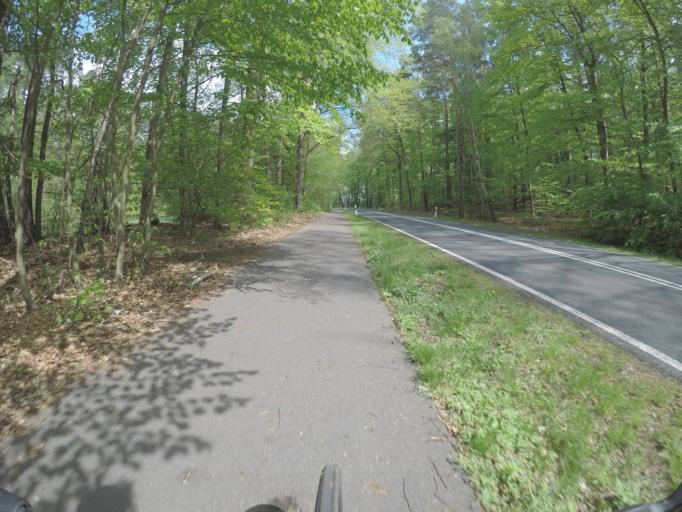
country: DE
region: Brandenburg
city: Joachimsthal
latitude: 52.9273
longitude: 13.7048
